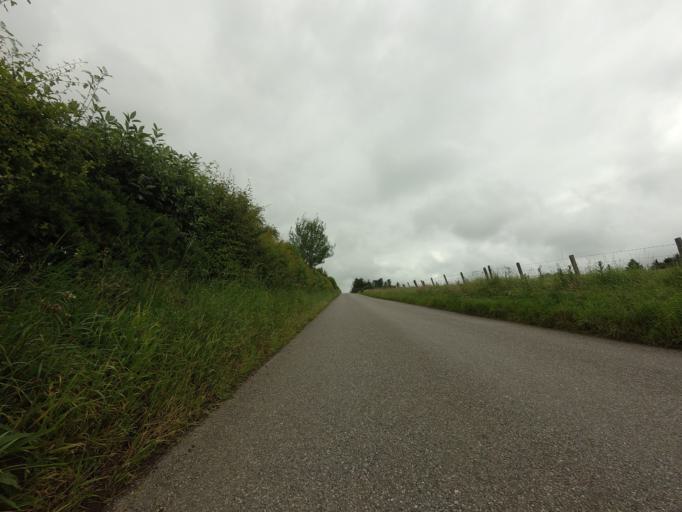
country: GB
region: Scotland
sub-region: Aberdeenshire
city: Mintlaw
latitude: 57.5254
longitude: -2.1417
